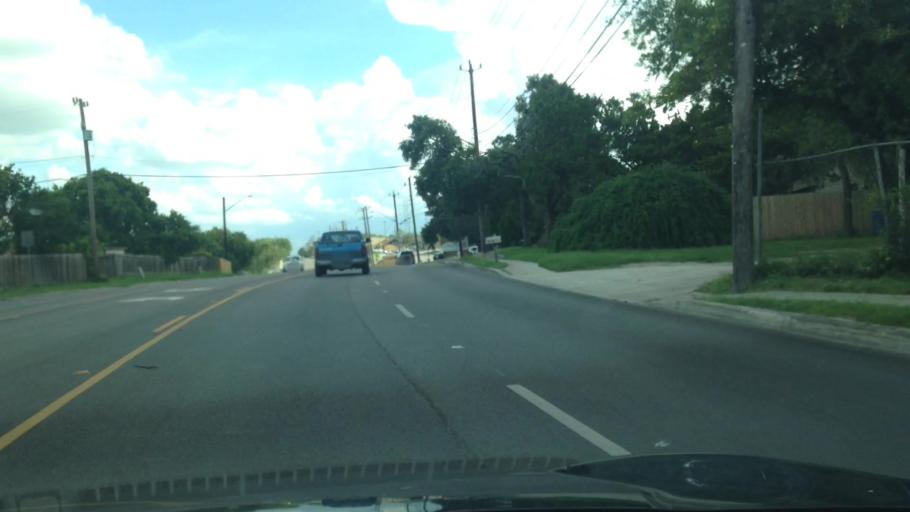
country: US
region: Texas
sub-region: Bexar County
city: Windcrest
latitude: 29.5711
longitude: -98.3963
